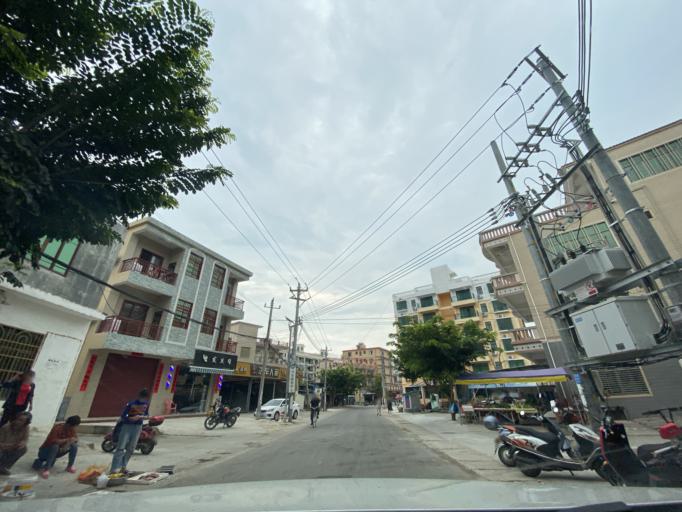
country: CN
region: Hainan
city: Yingzhou
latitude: 18.3933
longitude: 109.8439
